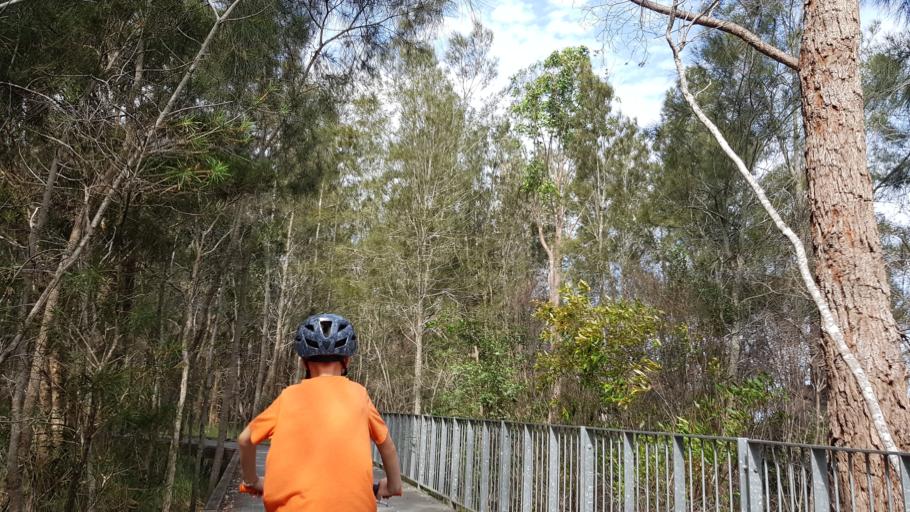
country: AU
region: New South Wales
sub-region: Pittwater
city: North Narrabeen
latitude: -33.7122
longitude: 151.2732
